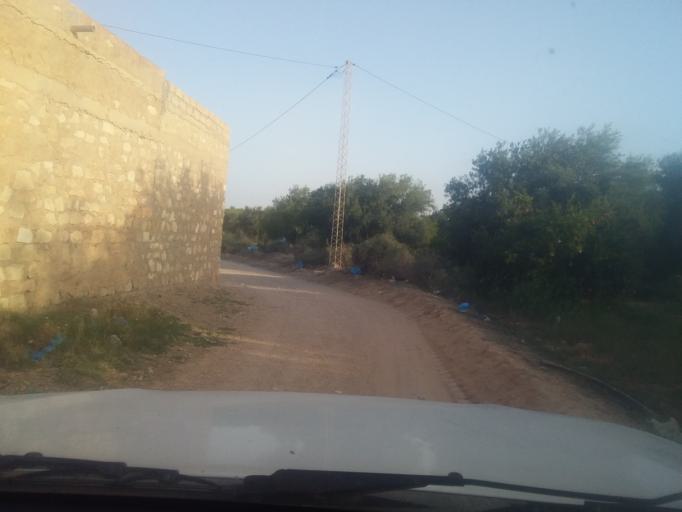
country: TN
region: Qabis
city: Gabes
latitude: 33.6316
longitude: 10.2937
